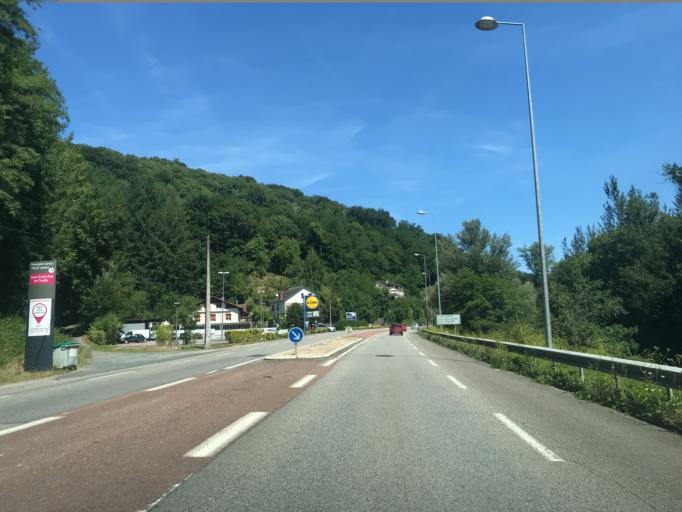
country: FR
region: Limousin
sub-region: Departement de la Correze
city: Tulle
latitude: 45.2466
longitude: 1.7462
